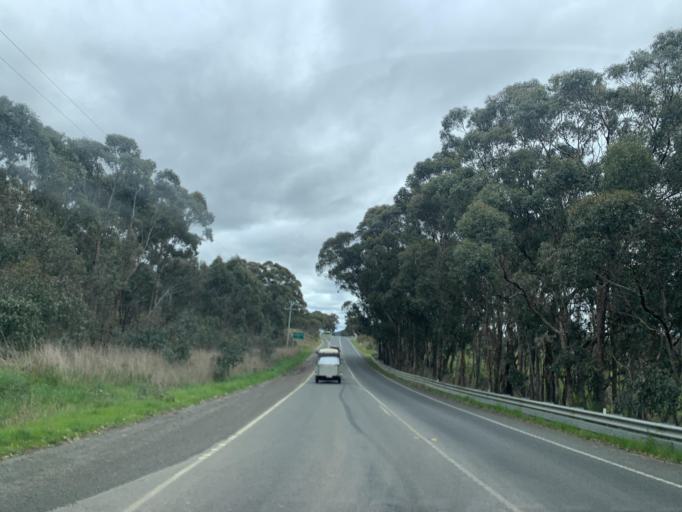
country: AU
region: Victoria
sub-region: Murrindindi
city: Kinglake West
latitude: -37.2067
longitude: 145.0753
